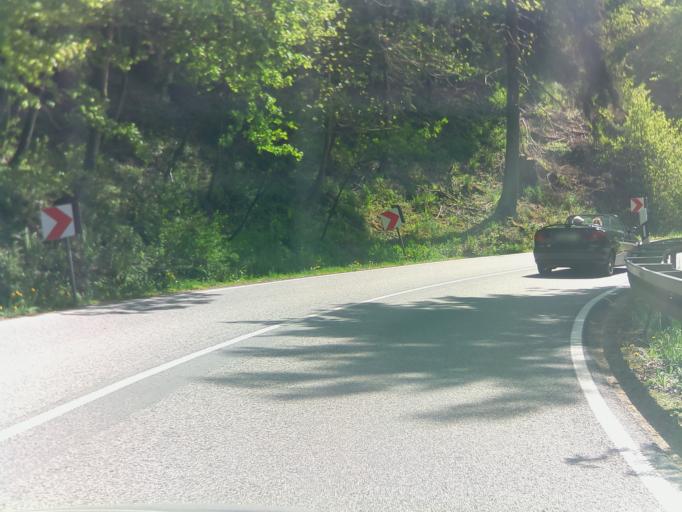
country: DE
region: Thuringia
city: Ilfeld
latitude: 51.6296
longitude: 10.8184
